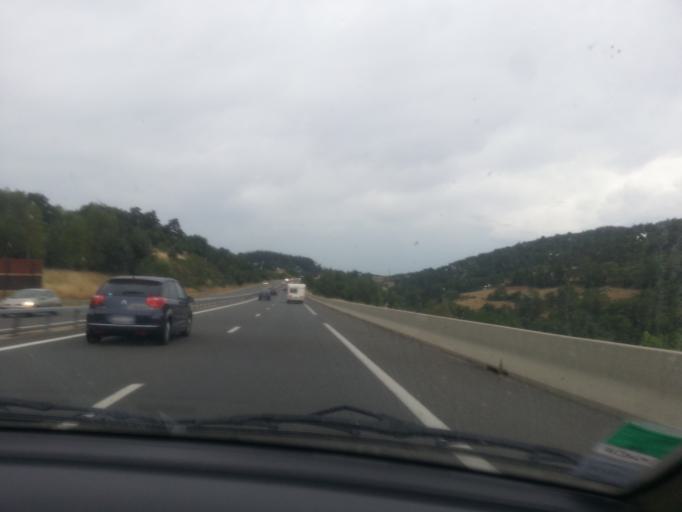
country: FR
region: Languedoc-Roussillon
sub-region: Departement de la Lozere
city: Marvejols
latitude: 44.5939
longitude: 3.2533
